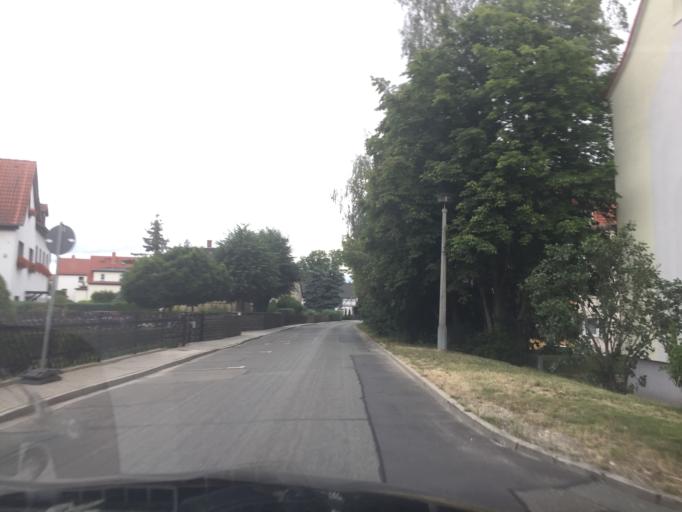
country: DE
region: Thuringia
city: Schmolln
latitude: 50.8894
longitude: 12.3543
